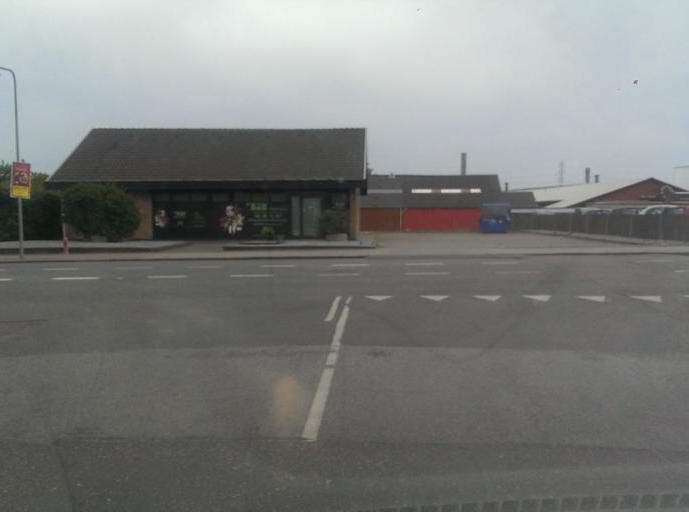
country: DK
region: South Denmark
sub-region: Esbjerg Kommune
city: Esbjerg
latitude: 55.4646
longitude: 8.4867
